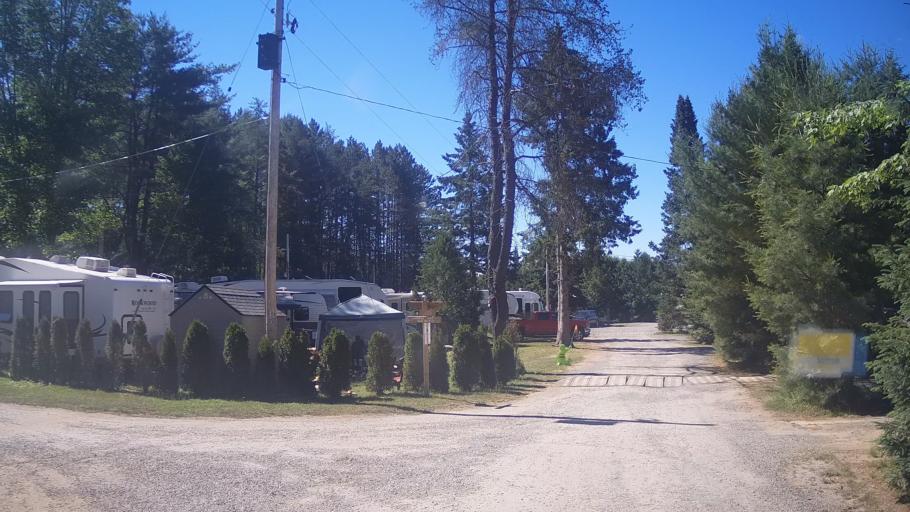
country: CA
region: Ontario
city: Huntsville
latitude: 45.3754
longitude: -79.2141
